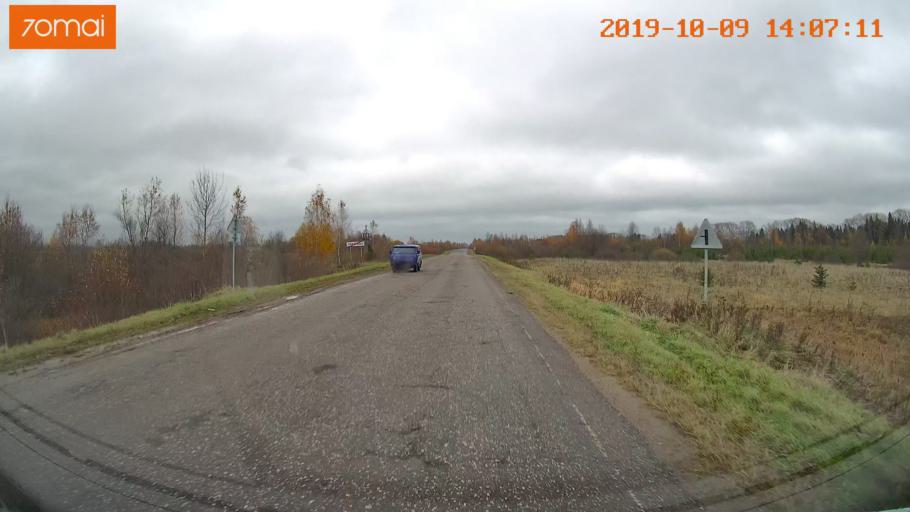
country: RU
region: Kostroma
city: Buy
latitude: 58.4689
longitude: 41.4195
